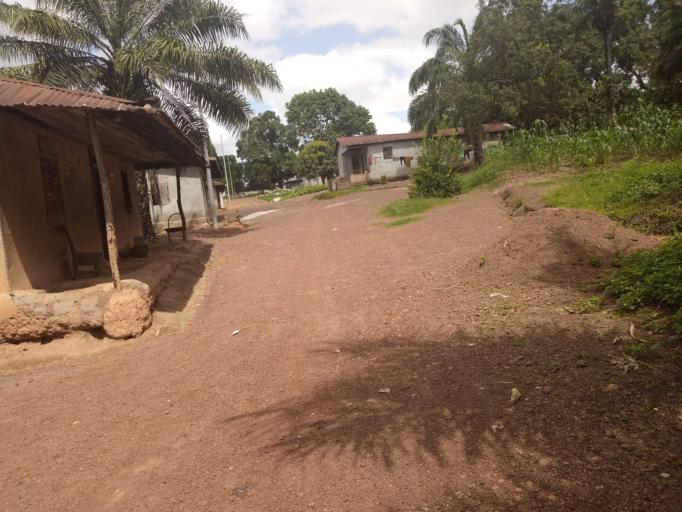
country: SL
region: Northern Province
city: Kamakwie
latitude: 9.4952
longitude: -12.2463
